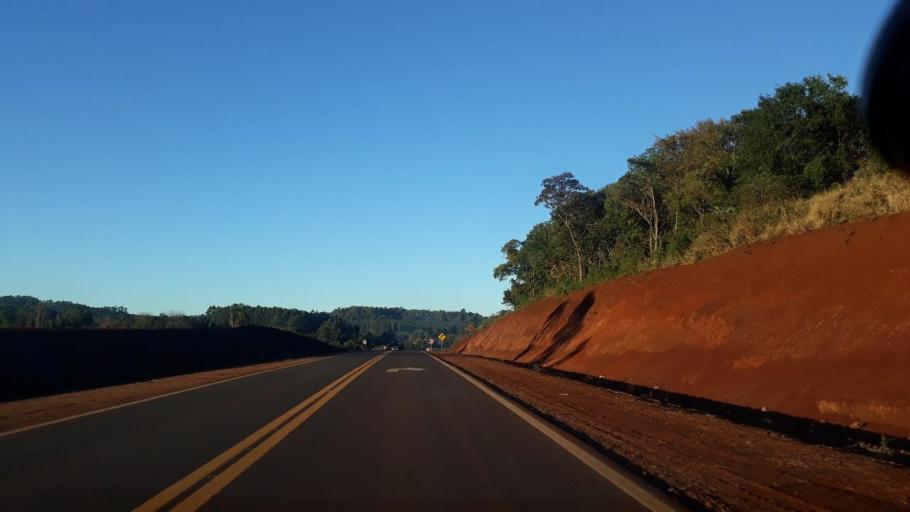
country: AR
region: Misiones
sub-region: Departamento de San Pedro
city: San Pedro
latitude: -26.5448
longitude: -53.9599
